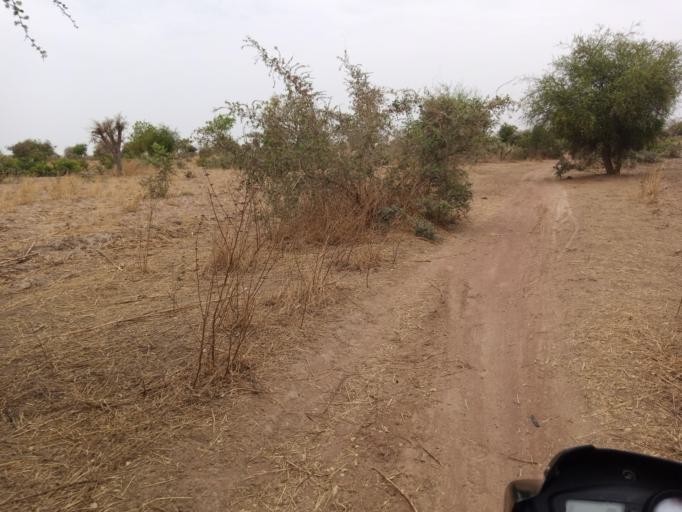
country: BF
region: Boucle du Mouhoun
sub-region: Province de la Kossi
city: Nouna
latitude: 12.8441
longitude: -4.0776
